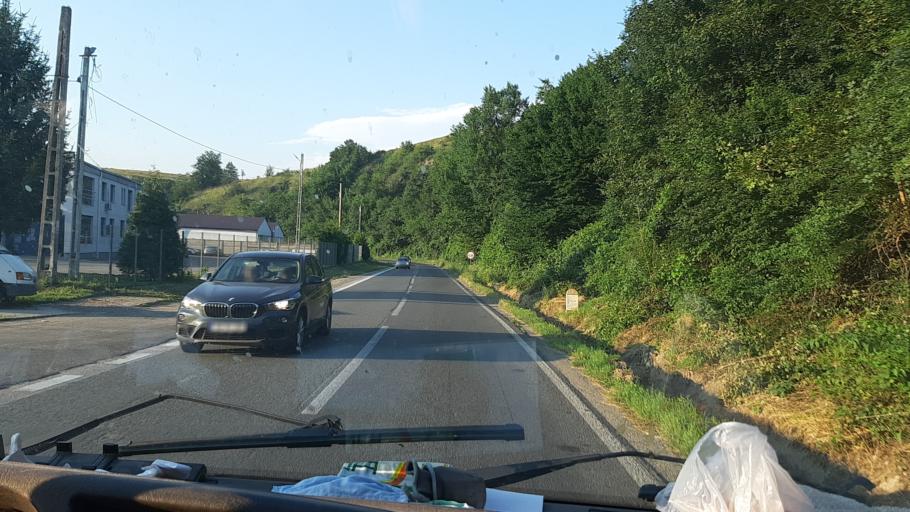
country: RO
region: Caras-Severin
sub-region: Municipiul Resita
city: Calnic
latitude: 45.3479
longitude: 21.8359
